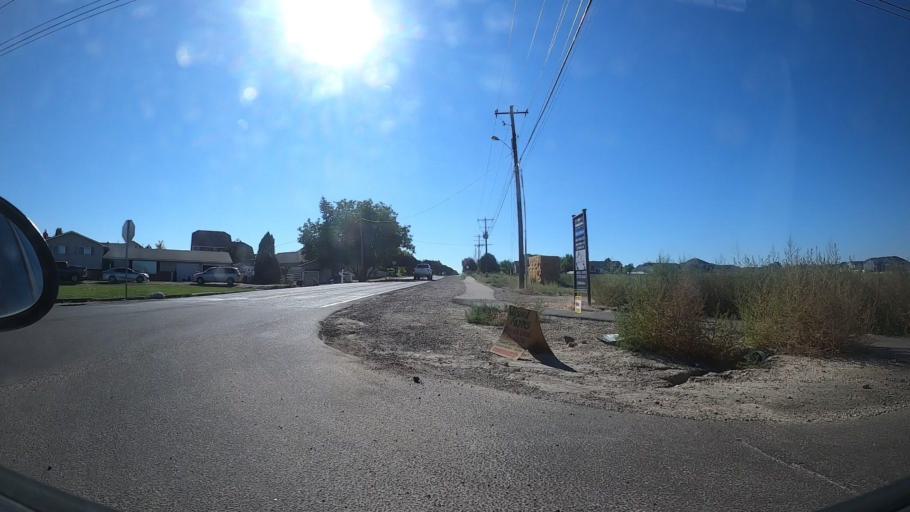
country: US
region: Idaho
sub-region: Canyon County
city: Nampa
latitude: 43.5562
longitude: -116.6128
